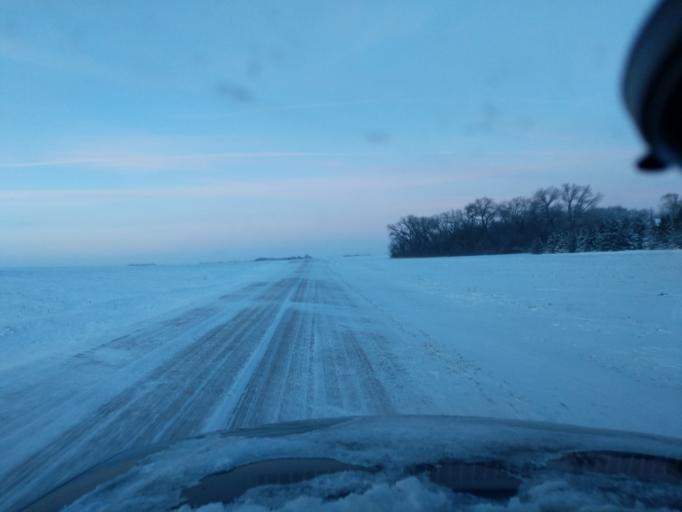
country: US
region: Minnesota
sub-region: Renville County
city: Renville
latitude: 44.7277
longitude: -95.3584
